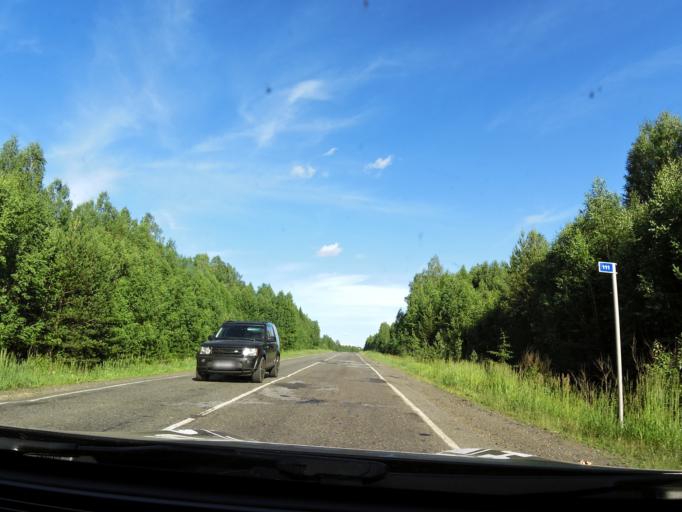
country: RU
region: Kirov
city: Dubrovka
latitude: 58.8991
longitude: 51.3075
